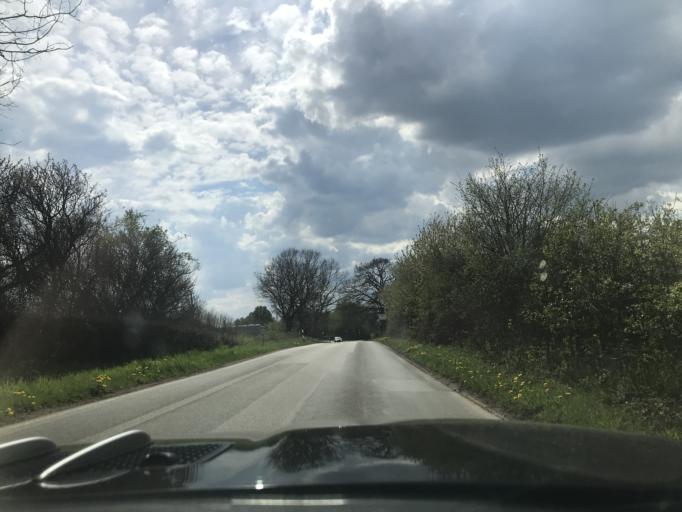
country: DE
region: Schleswig-Holstein
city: Timmendorfer Strand
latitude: 53.9632
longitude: 10.8175
